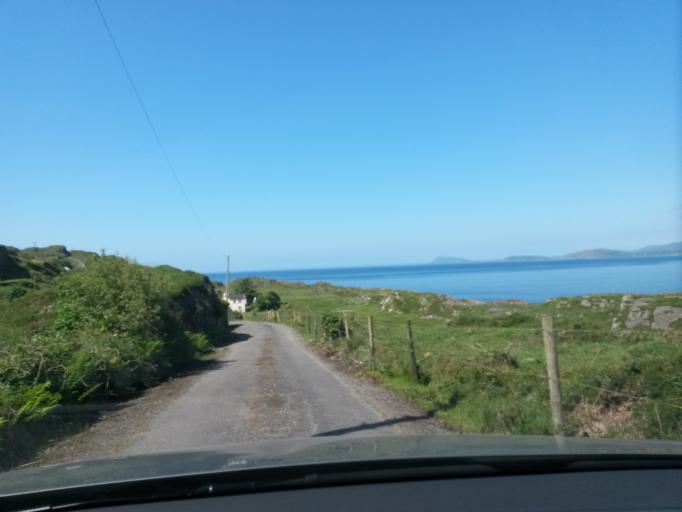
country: IE
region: Munster
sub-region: Ciarrai
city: Cahersiveen
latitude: 51.7293
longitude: -9.9761
